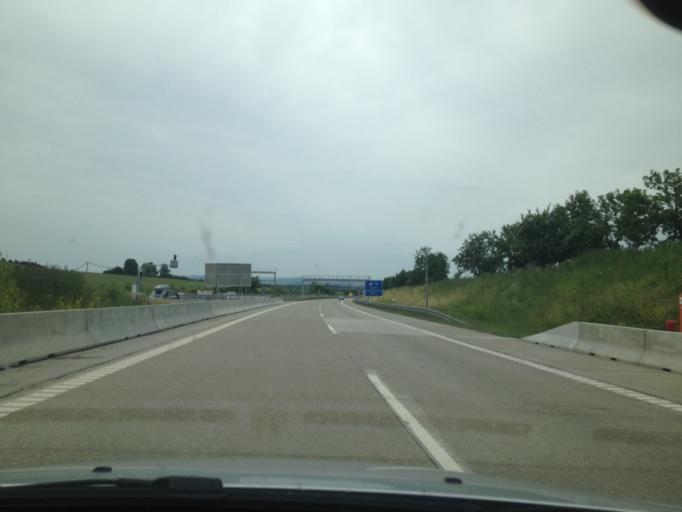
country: DE
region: Baden-Wuerttemberg
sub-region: Regierungsbezirk Stuttgart
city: Westhausen
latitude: 48.8750
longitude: 10.1672
